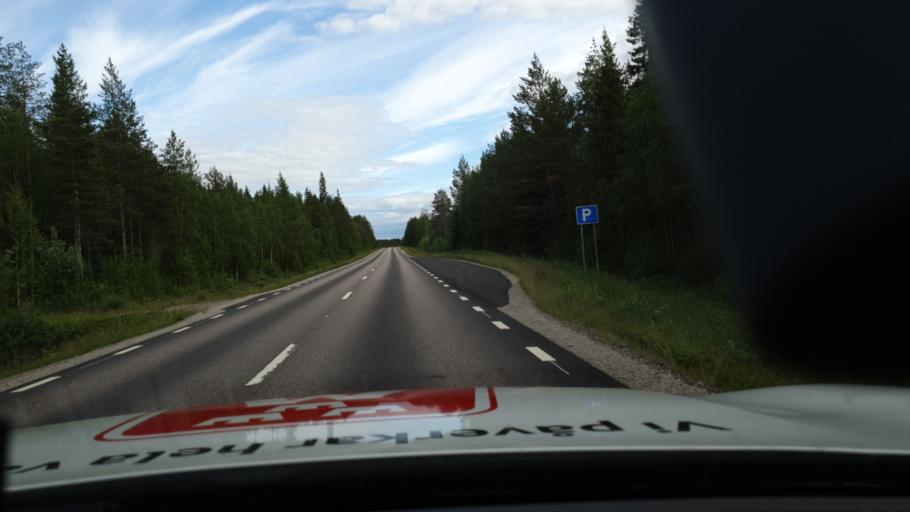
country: SE
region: Norrbotten
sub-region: Overkalix Kommun
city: OEverkalix
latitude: 66.3813
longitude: 22.8317
